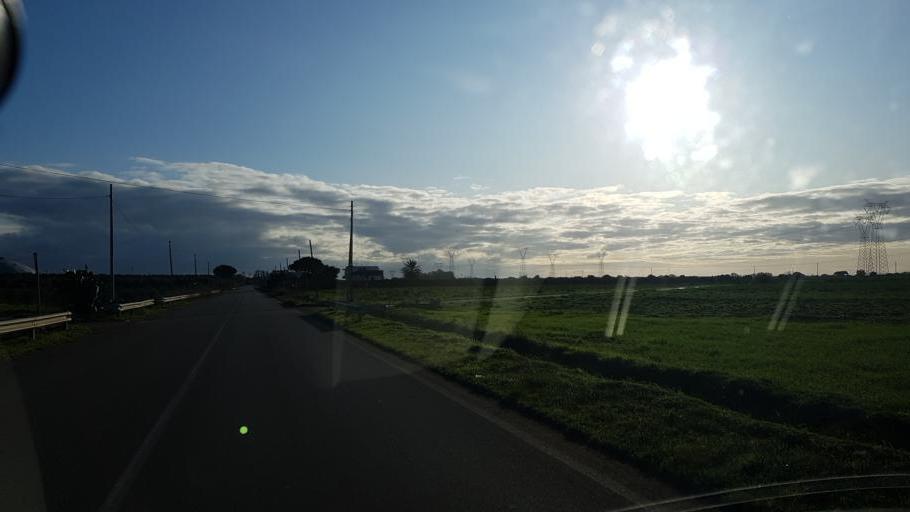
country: IT
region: Apulia
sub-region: Provincia di Brindisi
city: Tuturano
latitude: 40.5608
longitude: 18.0114
